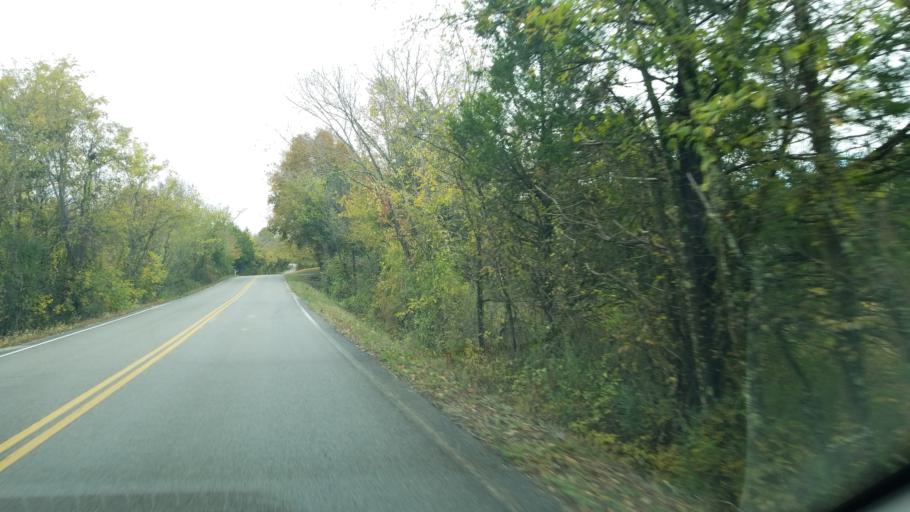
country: US
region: Tennessee
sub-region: Bradley County
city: Hopewell
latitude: 35.2498
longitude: -84.9826
